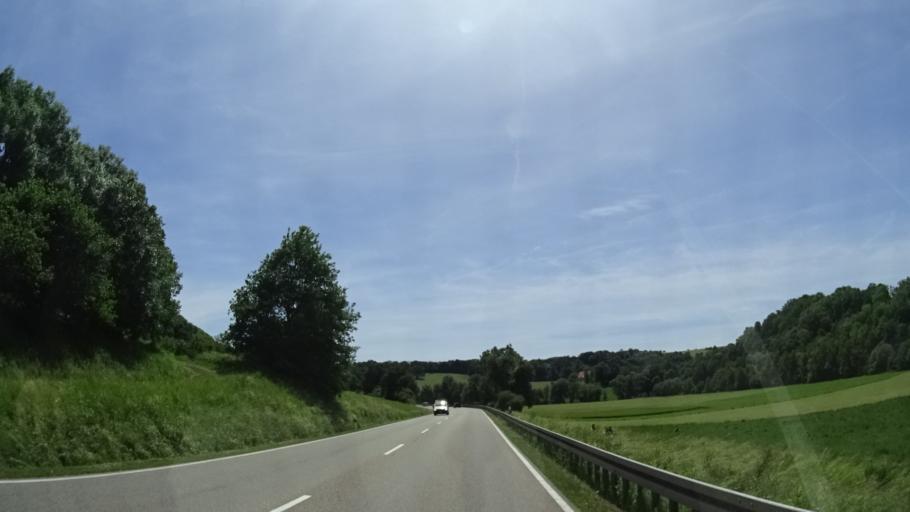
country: DE
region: Baden-Wuerttemberg
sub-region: Regierungsbezirk Stuttgart
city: Untermunkheim
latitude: 49.1448
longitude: 9.7322
